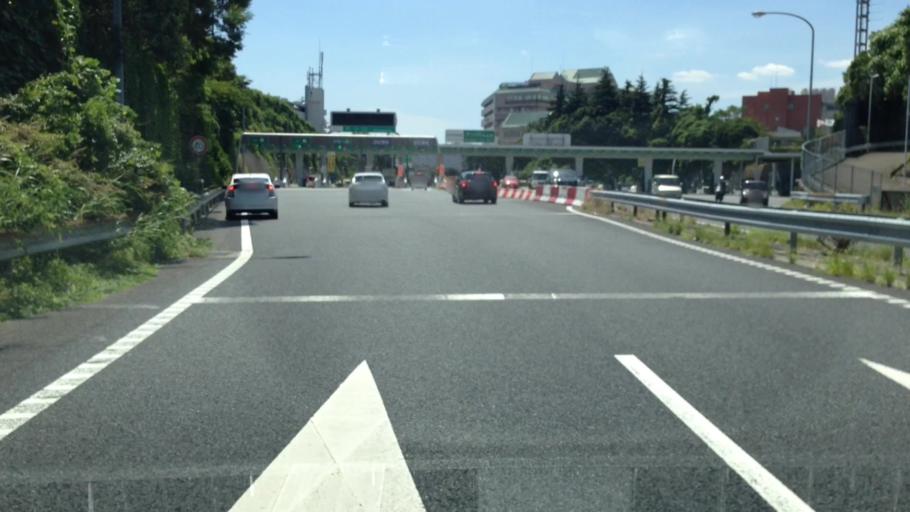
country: JP
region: Kanagawa
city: Yokohama
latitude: 35.4247
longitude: 139.5817
